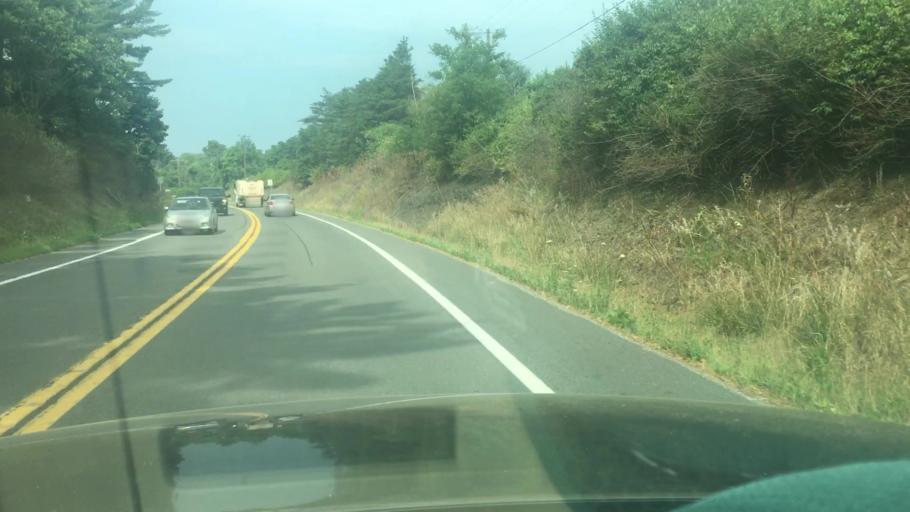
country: US
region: Pennsylvania
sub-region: Northumberland County
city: Elysburg
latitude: 40.8717
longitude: -76.5386
